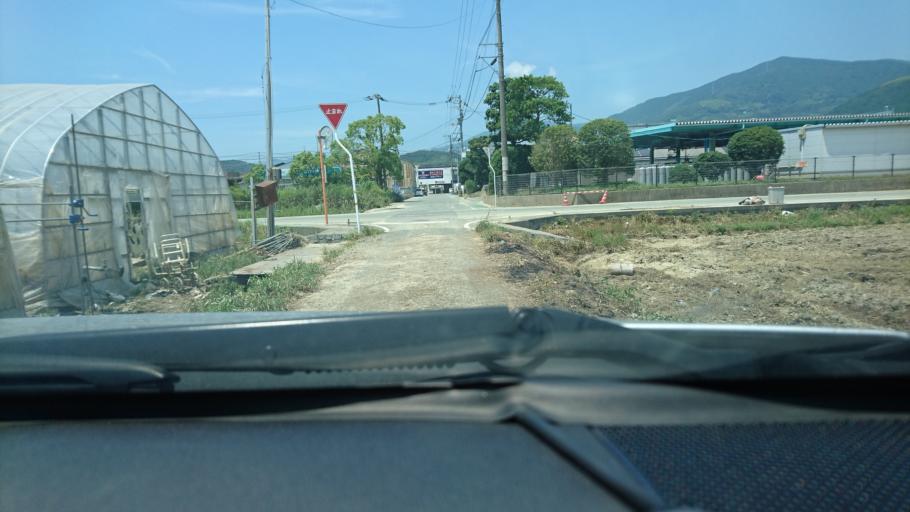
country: JP
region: Ehime
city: Ozu
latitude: 33.5264
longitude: 132.5674
